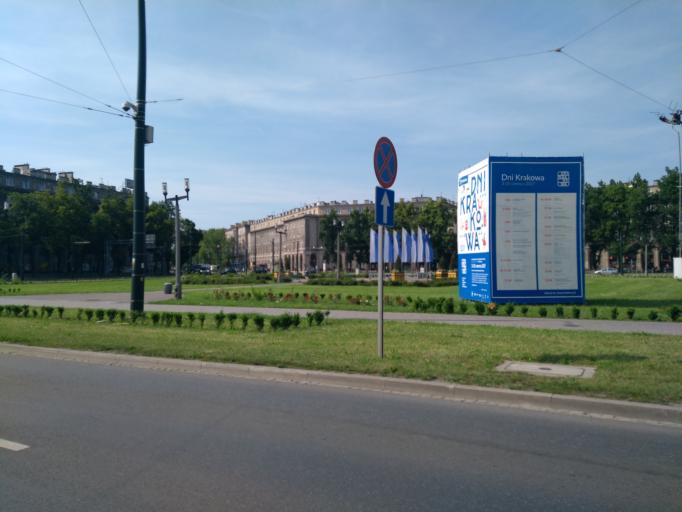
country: PL
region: Lesser Poland Voivodeship
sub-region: Powiat wielicki
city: Kokotow
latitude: 50.0716
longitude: 20.0376
